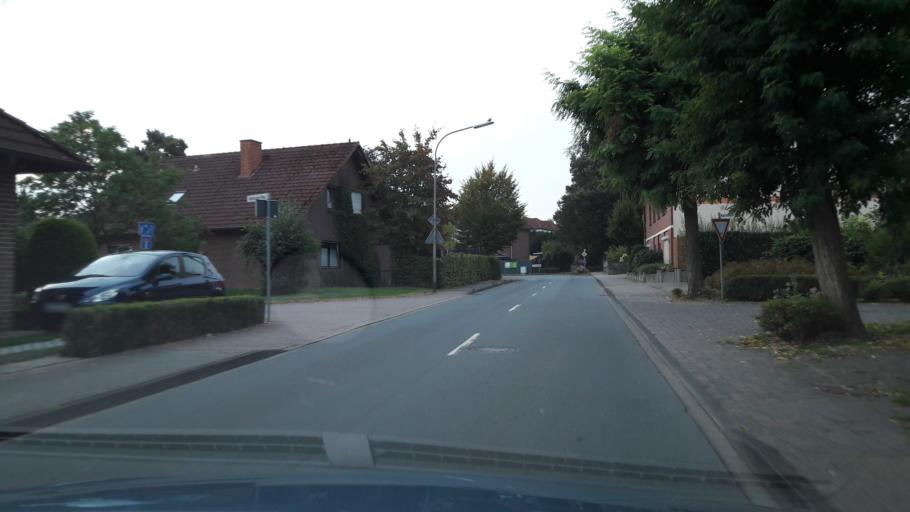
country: DE
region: North Rhine-Westphalia
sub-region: Regierungsbezirk Munster
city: Ennigerloh
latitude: 51.8383
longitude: 8.0199
